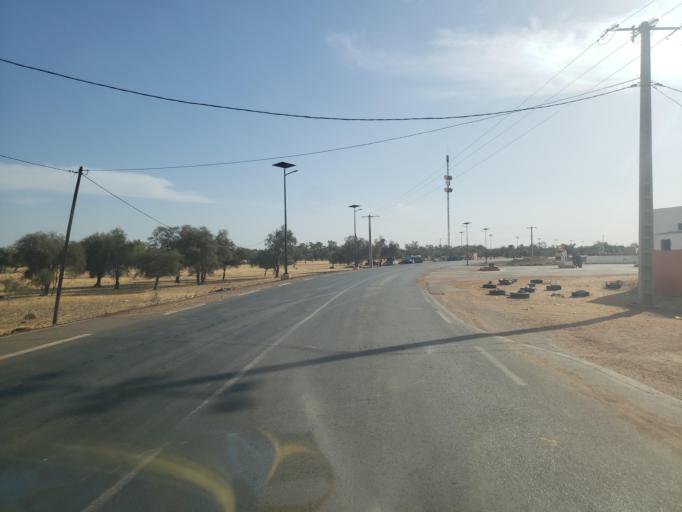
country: SN
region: Matam
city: Ranerou
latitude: 15.2961
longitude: -13.9574
